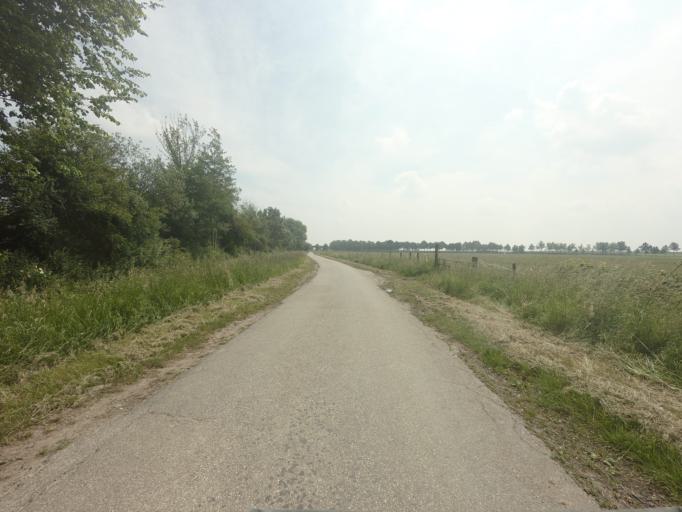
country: NL
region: Gelderland
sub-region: Gemeente Culemborg
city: Culemborg
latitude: 51.9893
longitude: 5.2409
